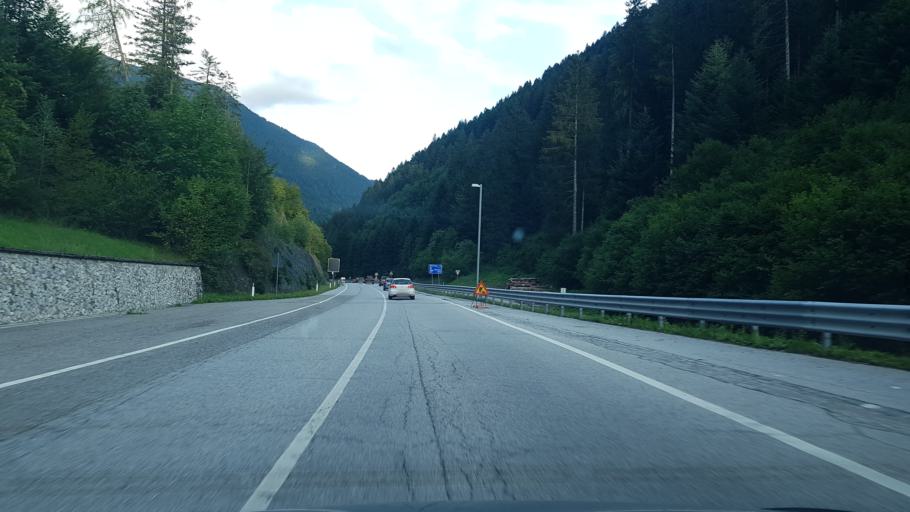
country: IT
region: Friuli Venezia Giulia
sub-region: Provincia di Udine
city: Rigolato
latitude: 46.5685
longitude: 12.8288
